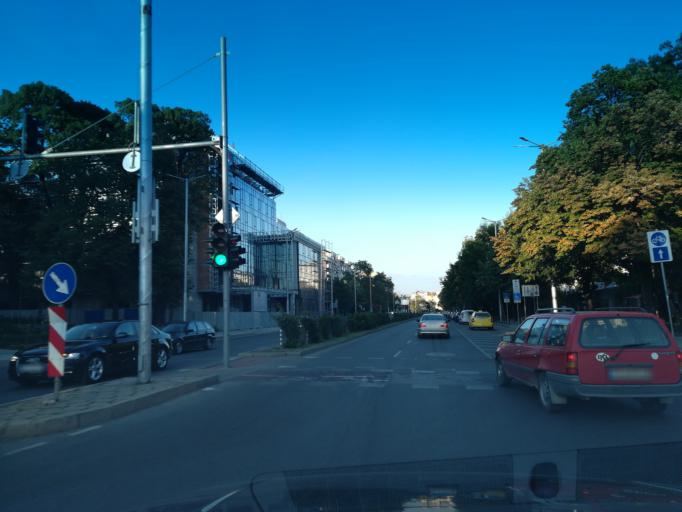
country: BG
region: Plovdiv
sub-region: Obshtina Plovdiv
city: Plovdiv
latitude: 42.1447
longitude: 24.7547
